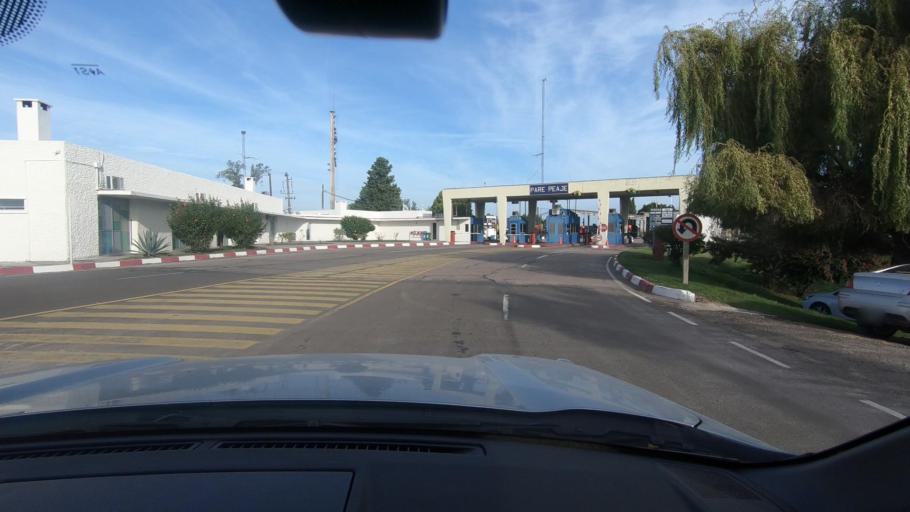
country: AR
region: Entre Rios
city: Colon
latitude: -32.2485
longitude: -58.1432
